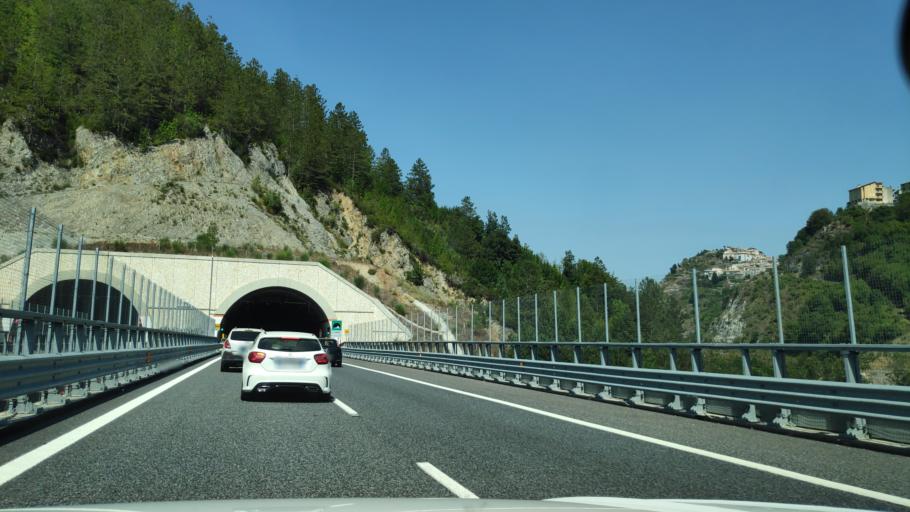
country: IT
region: Calabria
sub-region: Provincia di Cosenza
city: Mormanno
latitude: 39.8799
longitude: 15.9874
